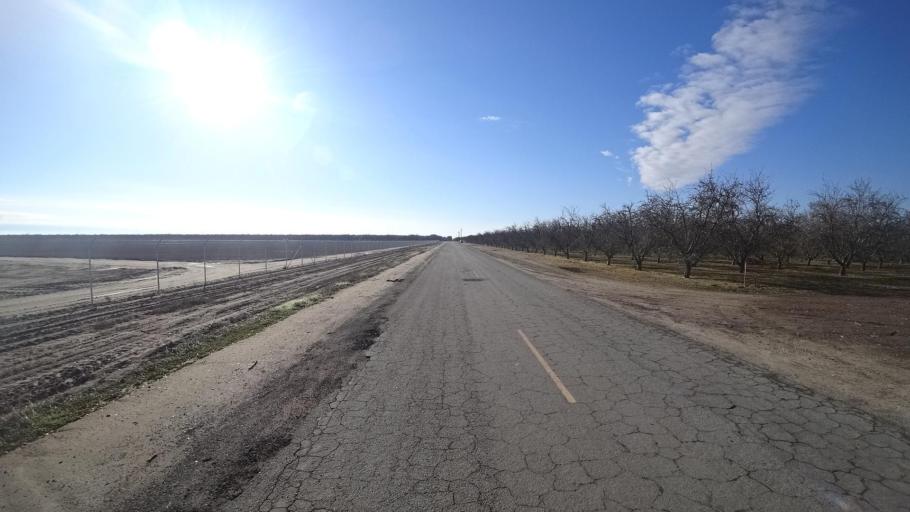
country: US
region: California
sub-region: Kern County
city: McFarland
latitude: 35.6923
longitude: -119.3120
